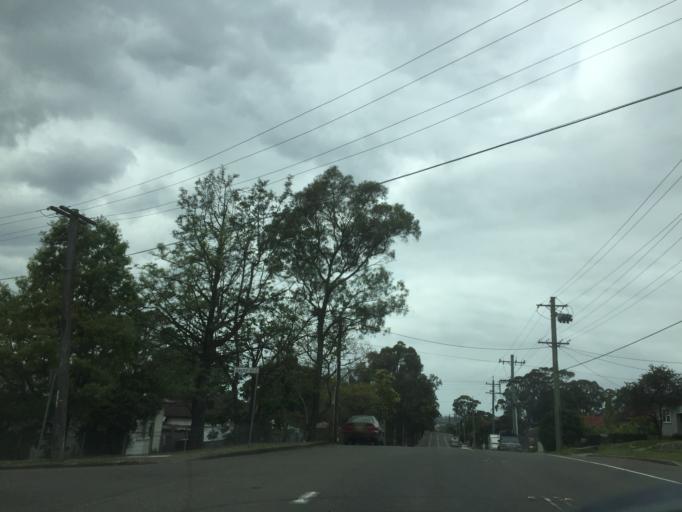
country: AU
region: New South Wales
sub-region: Blacktown
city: Blacktown
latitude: -33.7671
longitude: 150.9251
